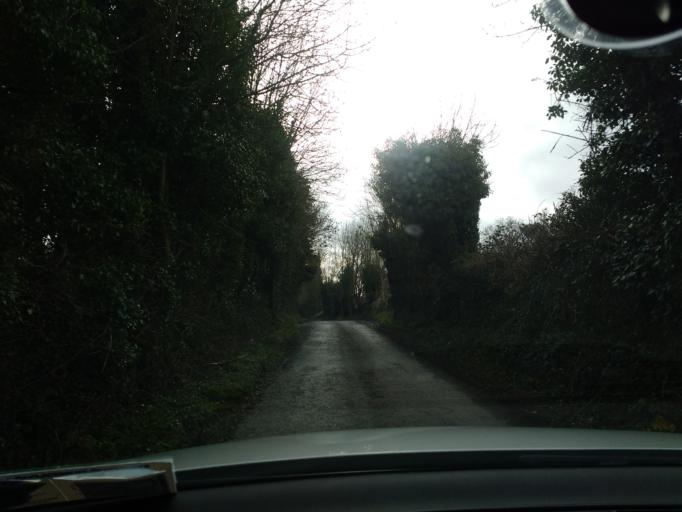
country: IE
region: Leinster
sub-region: Laois
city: Rathdowney
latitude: 52.6588
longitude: -7.5533
